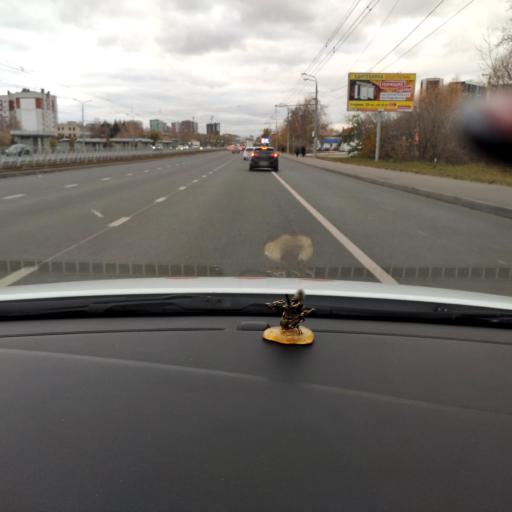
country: RU
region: Tatarstan
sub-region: Gorod Kazan'
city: Kazan
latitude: 55.7577
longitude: 49.1964
